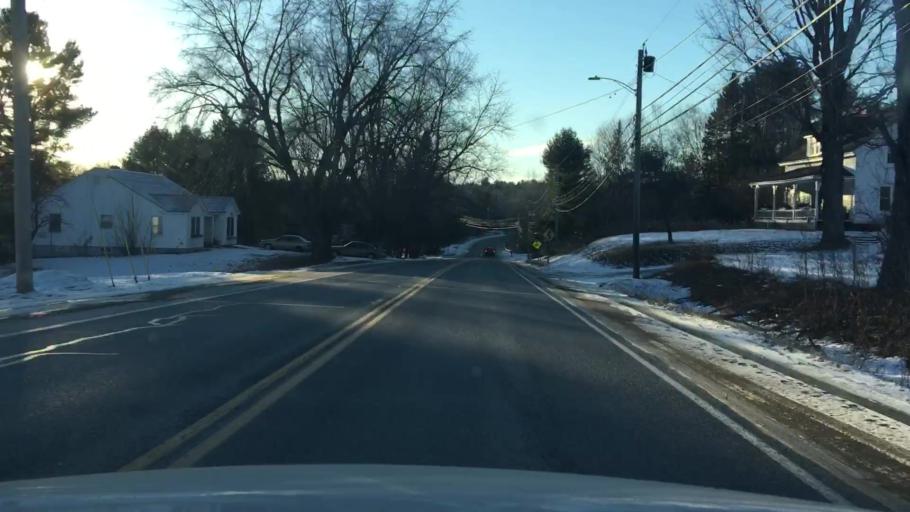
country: US
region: Maine
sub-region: Penobscot County
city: Eddington
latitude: 44.8184
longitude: -68.7040
